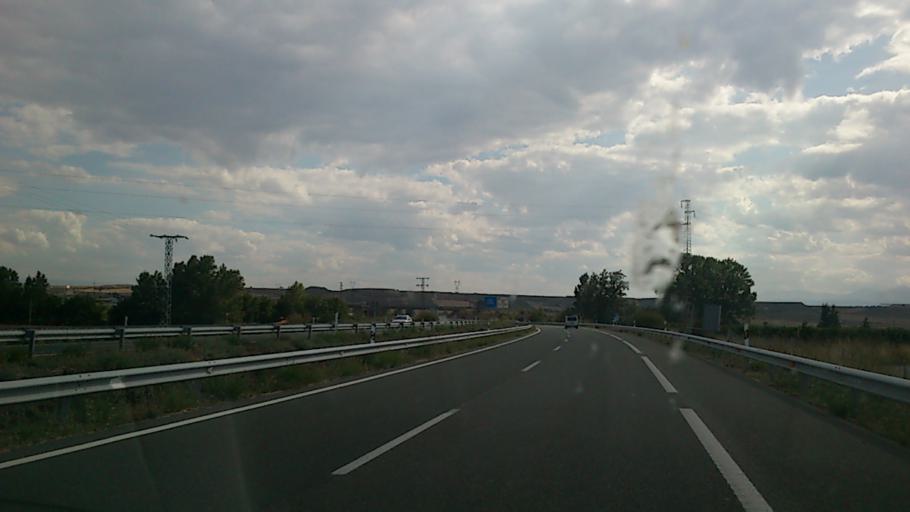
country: ES
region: La Rioja
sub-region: Provincia de La Rioja
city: Anguciana
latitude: 42.5669
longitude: -2.8804
